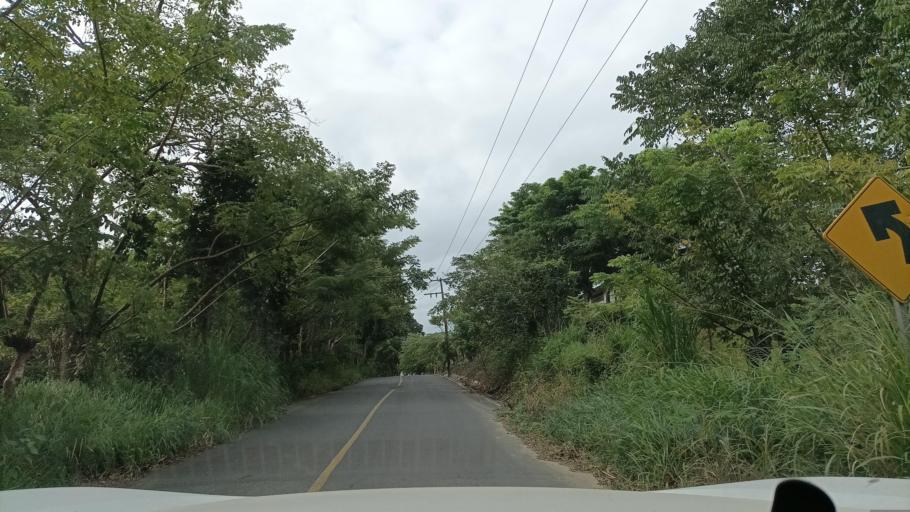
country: MX
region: Veracruz
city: Hidalgotitlan
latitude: 17.6974
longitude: -94.4686
